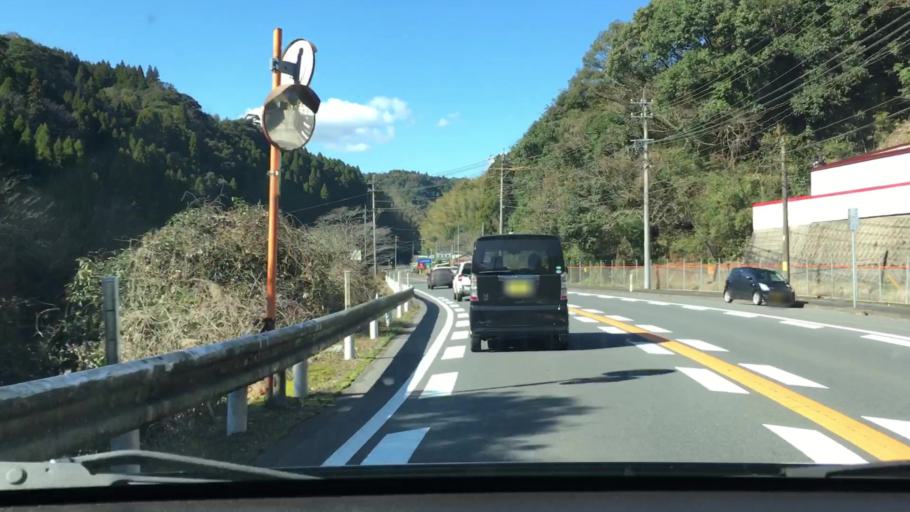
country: JP
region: Kagoshima
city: Kagoshima-shi
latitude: 31.6513
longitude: 130.5024
